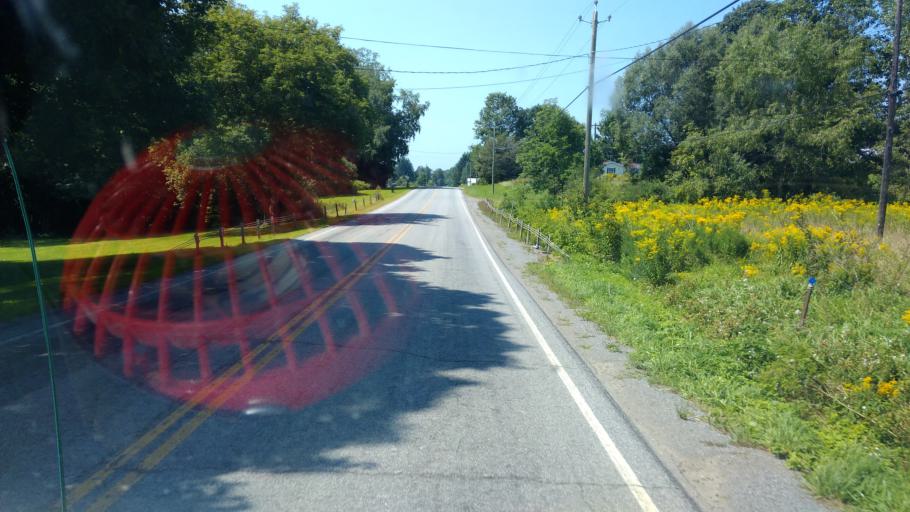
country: US
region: New York
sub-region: Allegany County
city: Belmont
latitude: 42.3029
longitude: -77.9753
